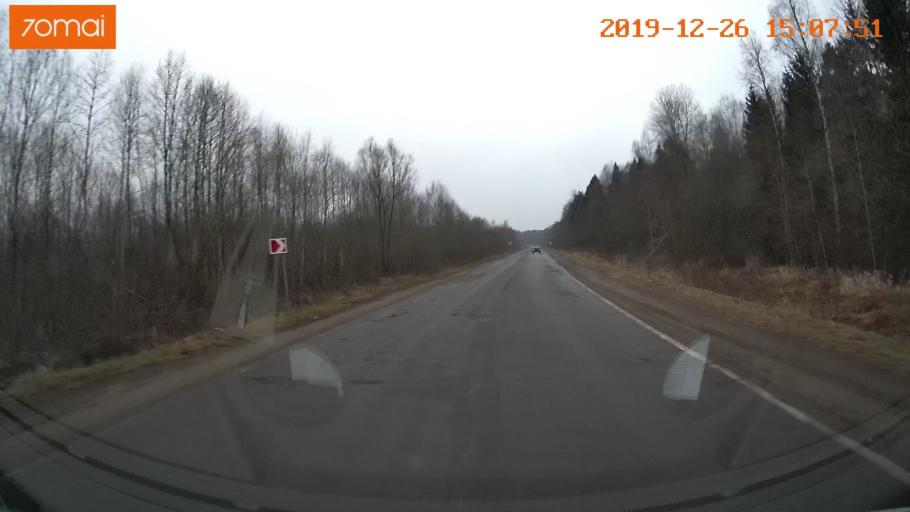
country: RU
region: Jaroslavl
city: Rybinsk
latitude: 58.1657
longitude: 38.8422
